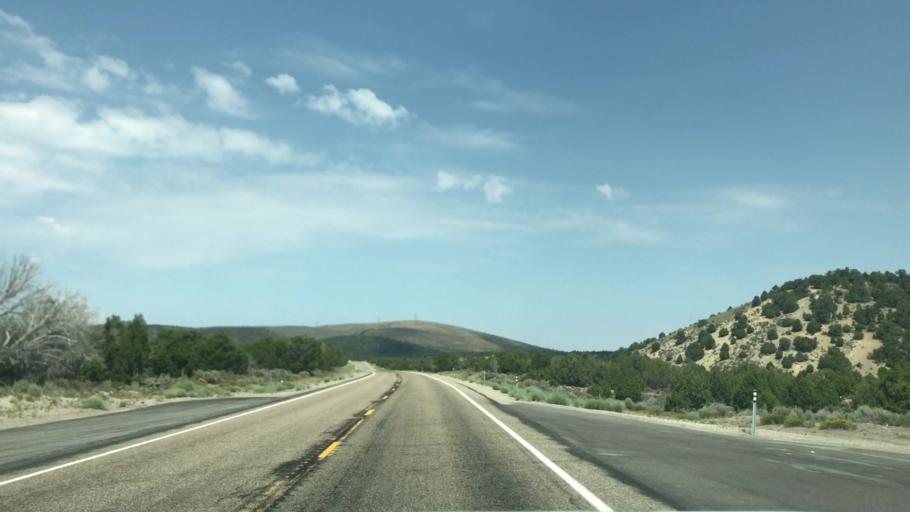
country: US
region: Nevada
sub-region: White Pine County
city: Ely
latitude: 39.3823
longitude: -115.0680
